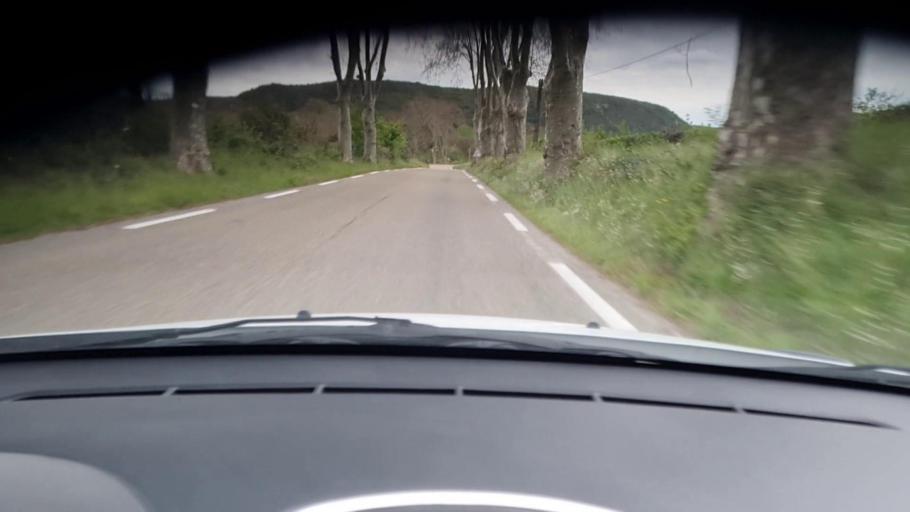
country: FR
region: Languedoc-Roussillon
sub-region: Departement du Gard
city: Blauzac
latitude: 43.9480
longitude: 4.3791
